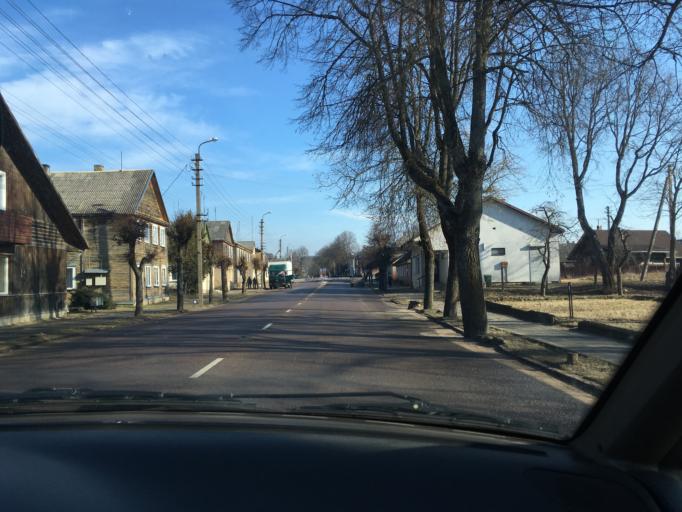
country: LT
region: Panevezys
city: Rokiskis
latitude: 55.7456
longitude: 25.8389
